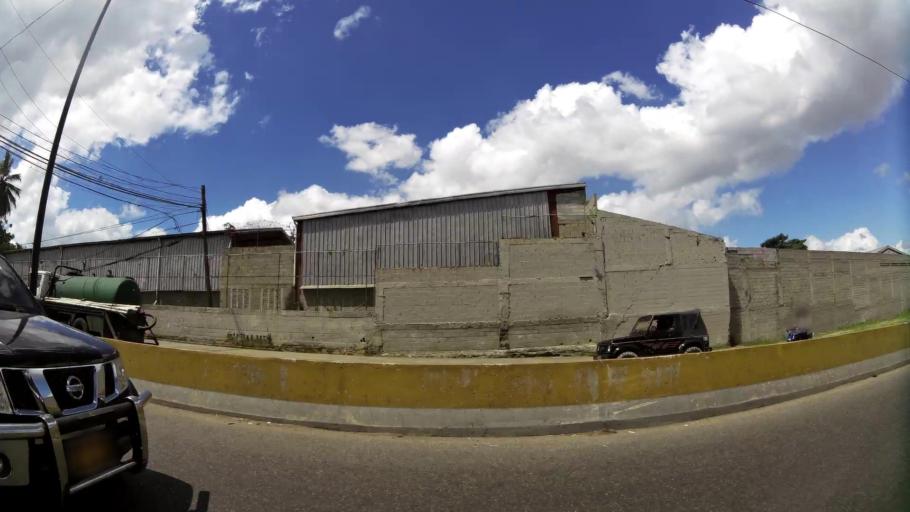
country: DO
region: Nacional
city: Ensanche Luperon
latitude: 18.5045
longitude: -69.9158
